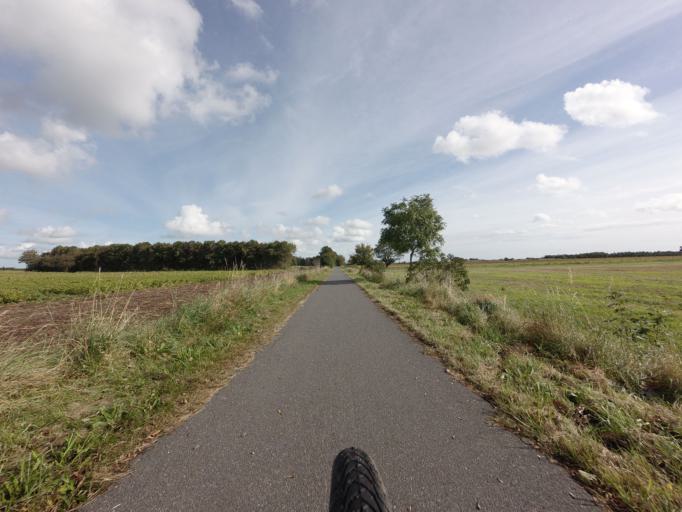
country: DK
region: Central Jutland
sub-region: Viborg Kommune
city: Bjerringbro
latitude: 56.4901
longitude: 9.6426
